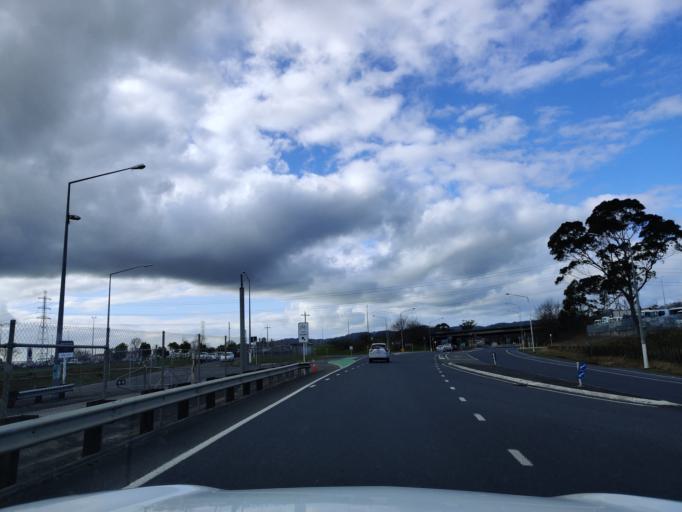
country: NZ
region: Auckland
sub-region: Auckland
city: Papakura
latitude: -37.1086
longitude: 174.9441
